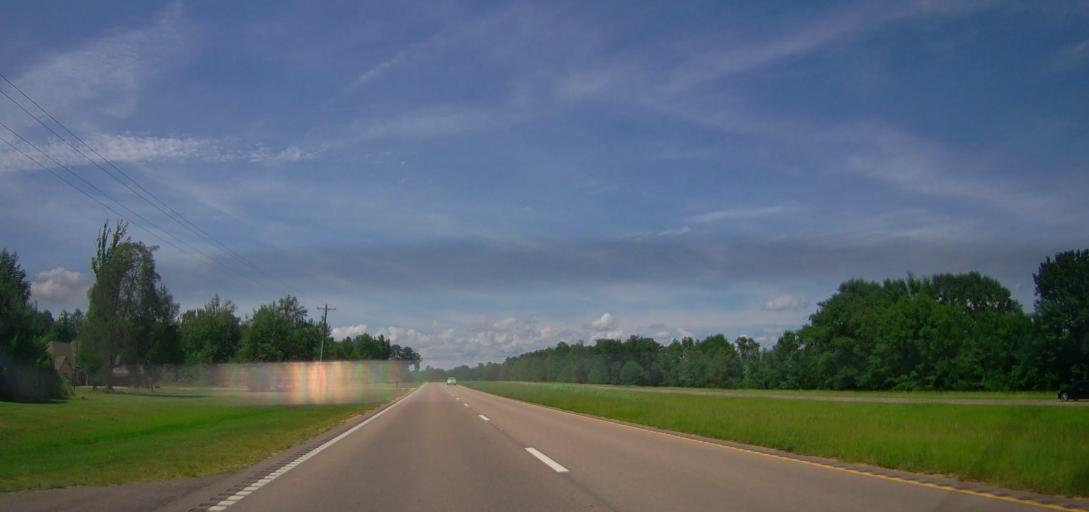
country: US
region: Mississippi
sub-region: Monroe County
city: Aberdeen
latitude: 33.9326
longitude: -88.5968
